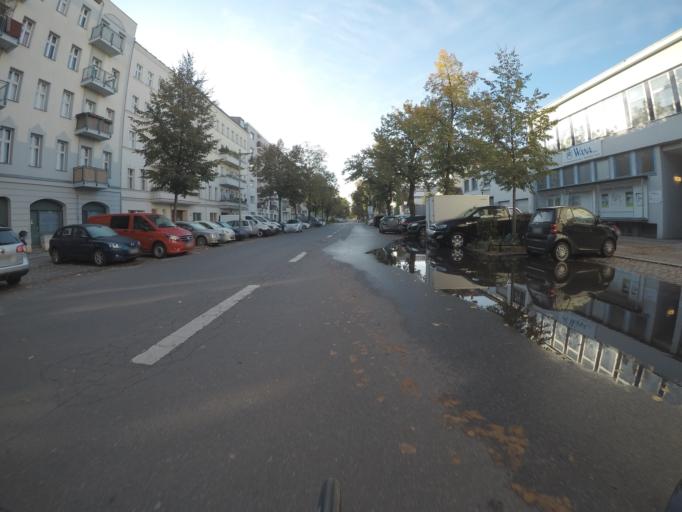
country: DE
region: Berlin
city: Charlottenburg Bezirk
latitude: 52.5141
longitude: 13.2881
